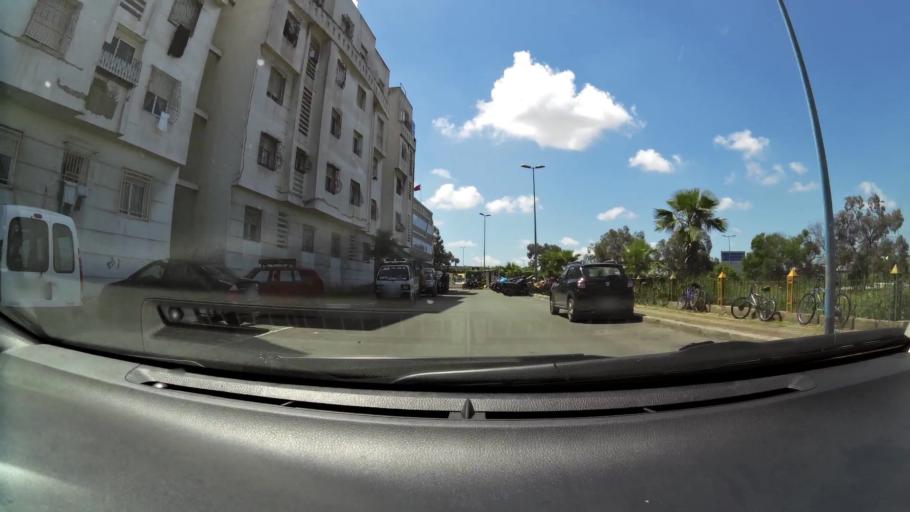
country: MA
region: Grand Casablanca
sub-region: Casablanca
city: Casablanca
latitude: 33.5610
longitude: -7.5859
